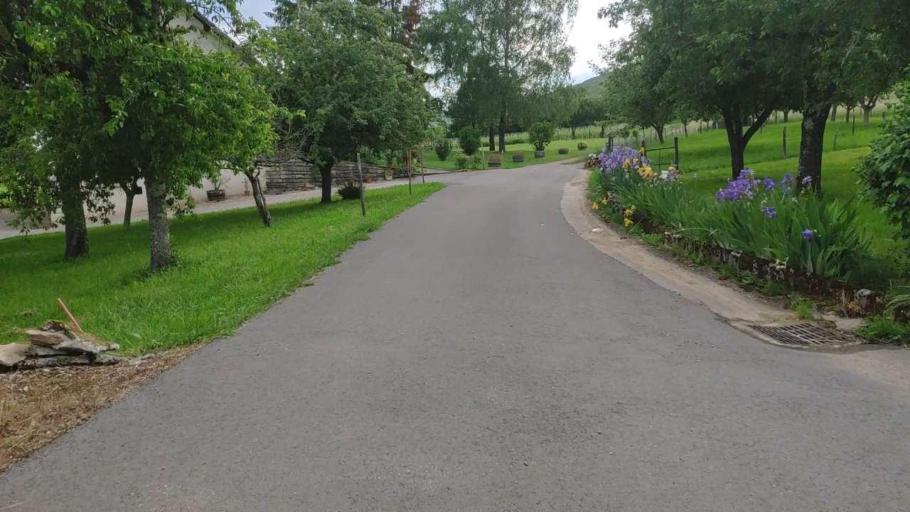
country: FR
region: Franche-Comte
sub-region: Departement du Jura
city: Perrigny
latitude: 46.7190
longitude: 5.5974
